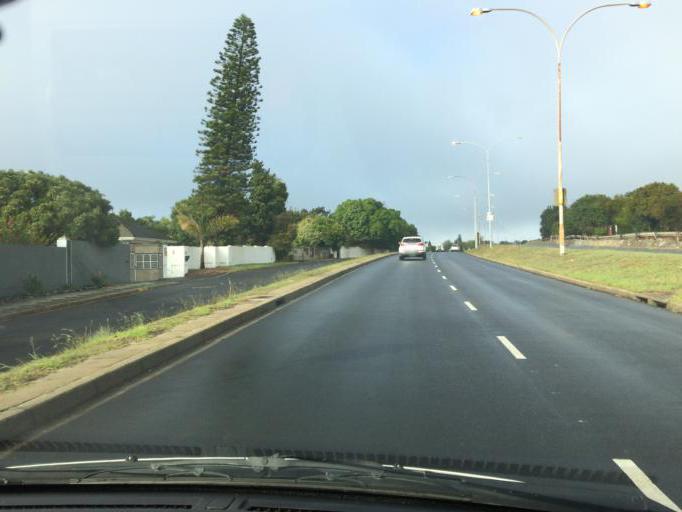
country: ZA
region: Western Cape
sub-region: City of Cape Town
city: Kraaifontein
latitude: -33.8404
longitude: 18.6485
